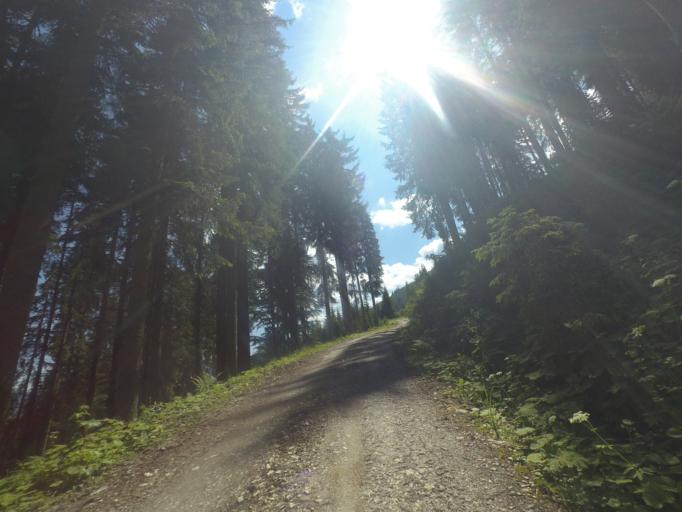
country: AT
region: Salzburg
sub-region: Politischer Bezirk Sankt Johann im Pongau
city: Schwarzach im Pongau
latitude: 47.3047
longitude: 13.1622
